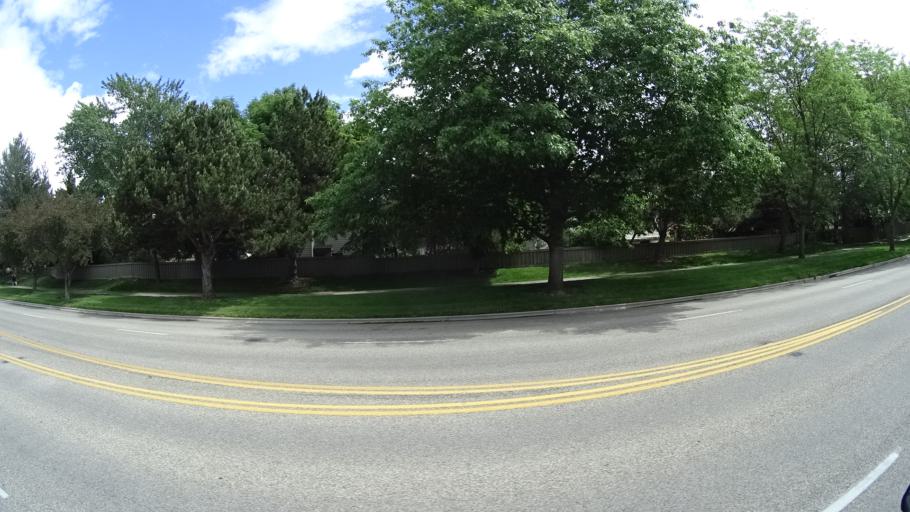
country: US
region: Idaho
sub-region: Ada County
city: Boise
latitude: 43.5803
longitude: -116.1621
